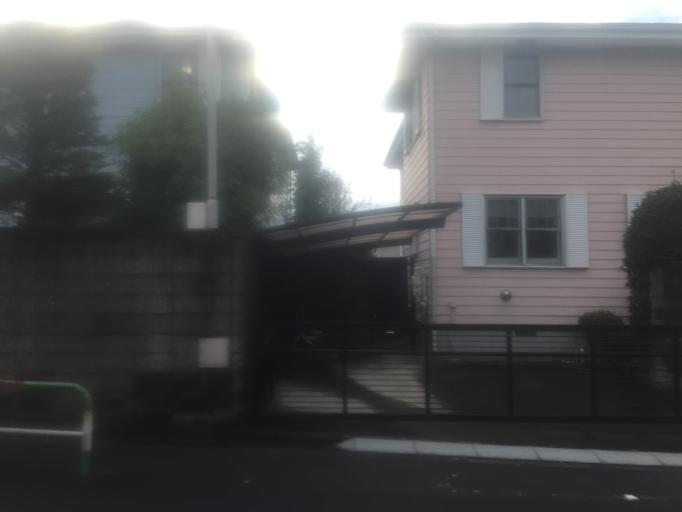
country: JP
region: Tokyo
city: Tokyo
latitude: 35.6022
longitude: 139.6650
